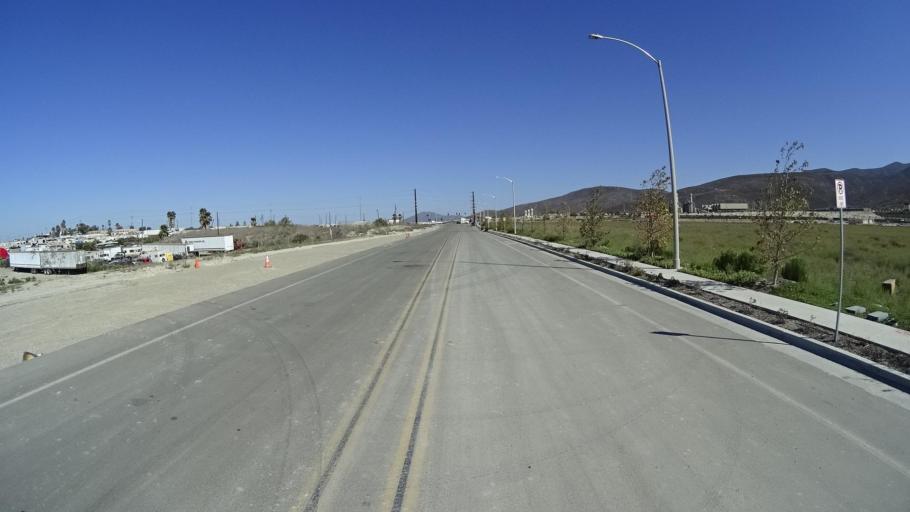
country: MX
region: Baja California
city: Tijuana
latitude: 32.5644
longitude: -116.9187
